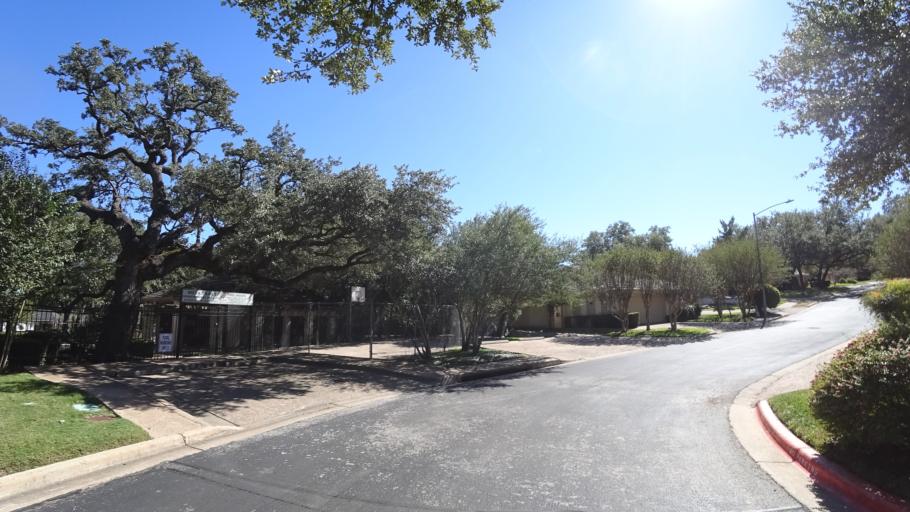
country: US
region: Texas
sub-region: Williamson County
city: Jollyville
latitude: 30.3682
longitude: -97.7571
